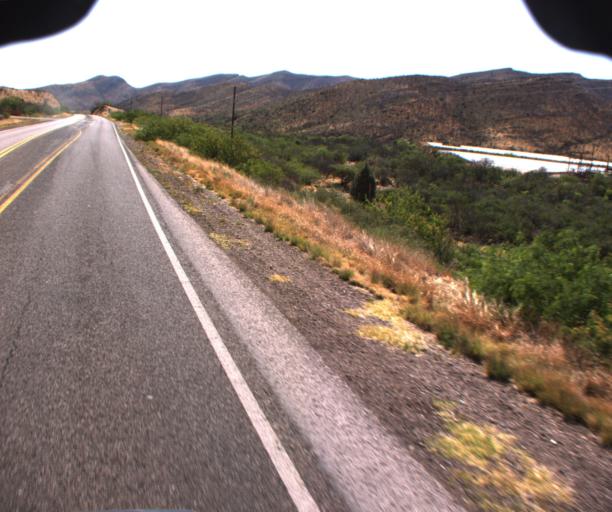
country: US
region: Arizona
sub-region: Cochise County
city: Bisbee
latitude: 31.4298
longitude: -109.8702
